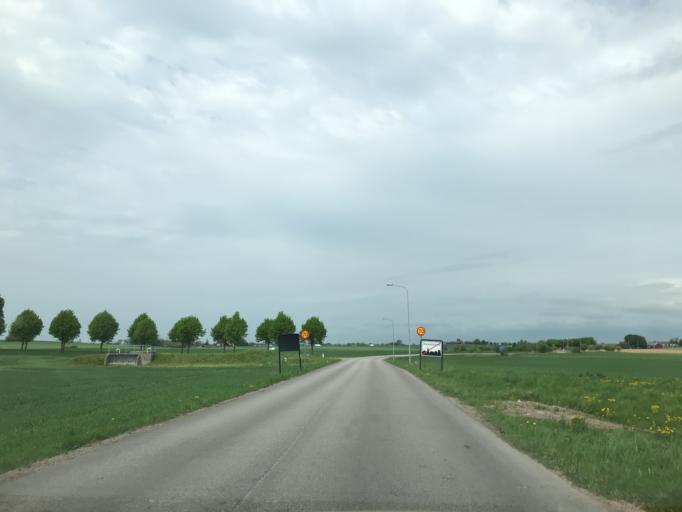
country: SE
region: Skane
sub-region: Svalovs Kommun
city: Svaloev
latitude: 55.8717
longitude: 13.1570
